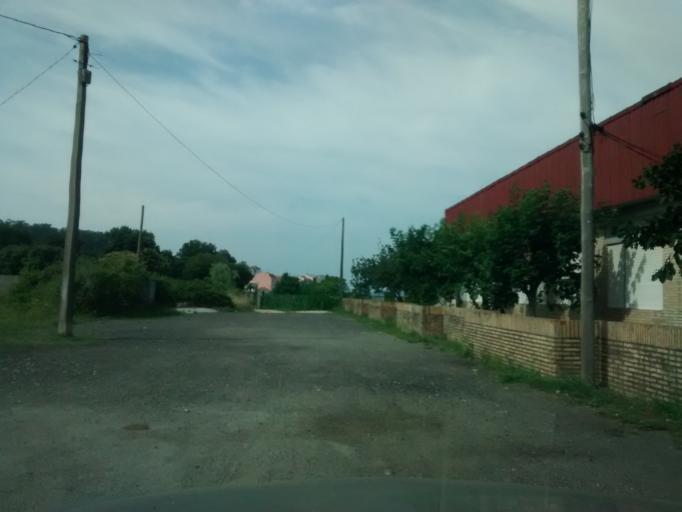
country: ES
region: Galicia
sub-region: Provincia de Pontevedra
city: O Grove
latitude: 42.4809
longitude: -8.8609
